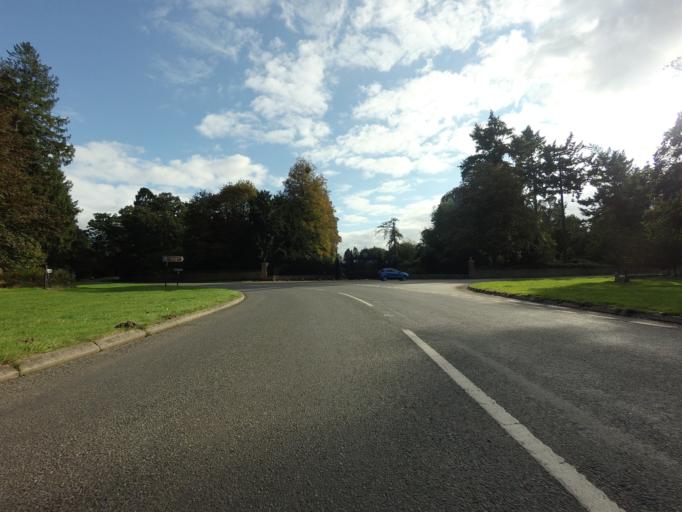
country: GB
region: England
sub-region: Norfolk
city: Dersingham
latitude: 52.8331
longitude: 0.5126
